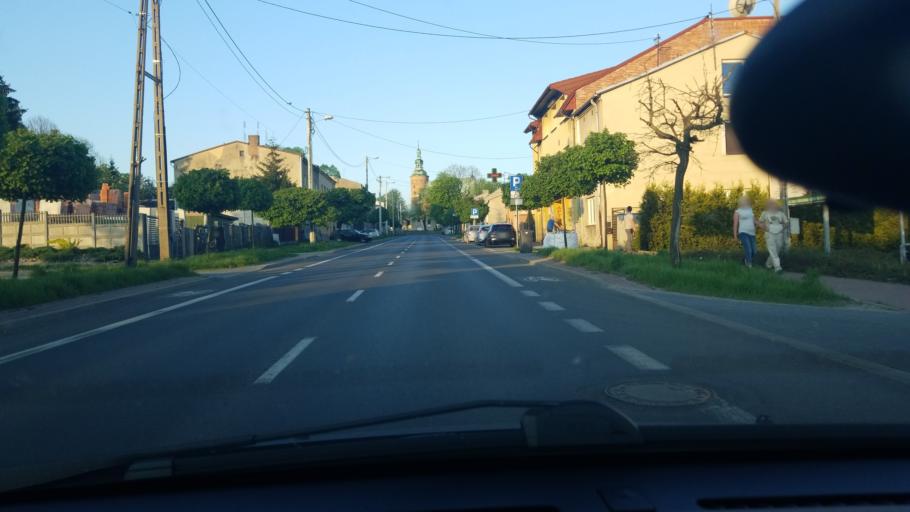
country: PL
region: Silesian Voivodeship
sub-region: Czestochowa
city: Czestochowa
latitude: 50.8040
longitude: 19.0908
